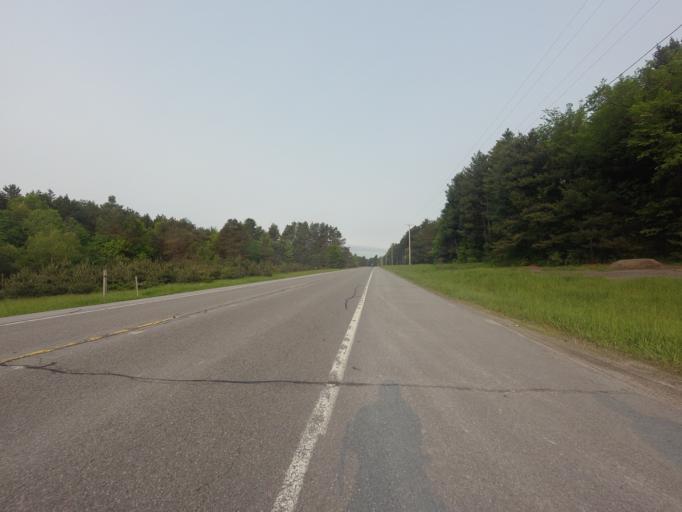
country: US
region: New York
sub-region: Jefferson County
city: Carthage
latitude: 44.0680
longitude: -75.5199
